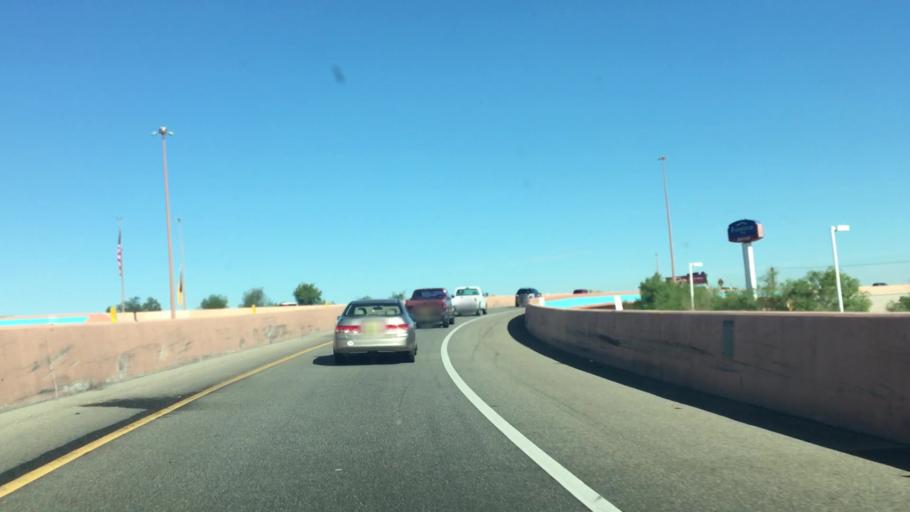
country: US
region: New Mexico
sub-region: Bernalillo County
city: Albuquerque
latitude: 35.1067
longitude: -106.6264
